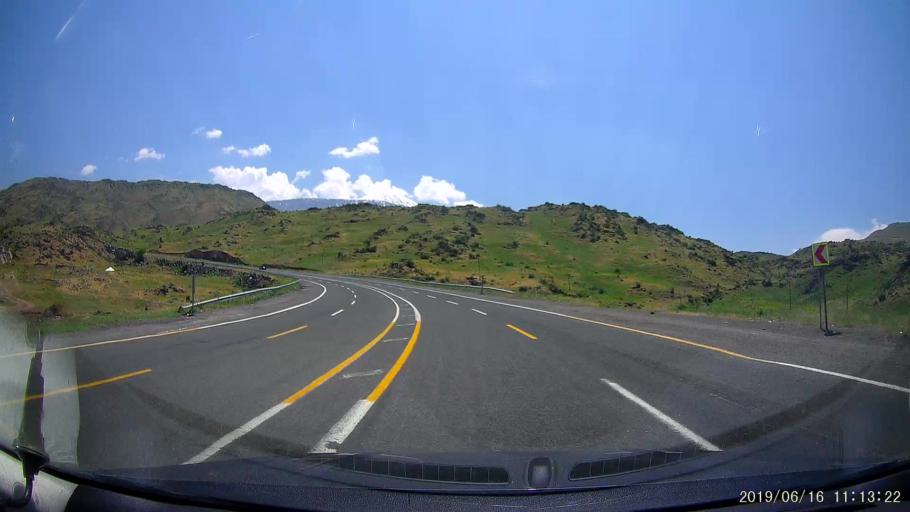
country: TR
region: Igdir
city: Igdir
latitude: 39.7847
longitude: 44.1363
